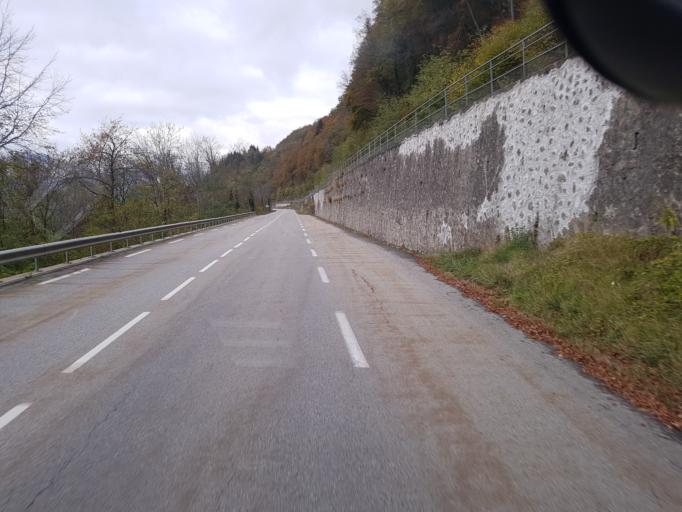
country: FR
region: Rhone-Alpes
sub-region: Departement de l'Isere
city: La Motte-Saint-Martin
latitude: 44.9385
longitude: 5.6404
